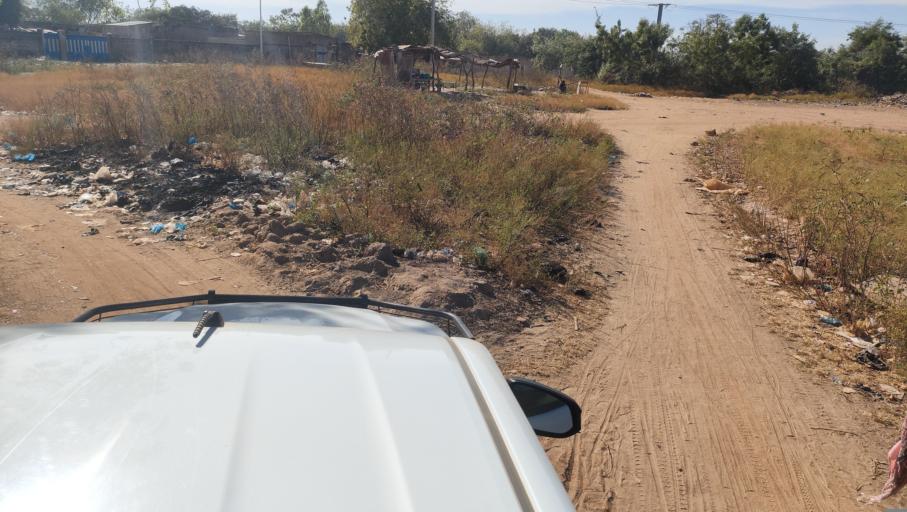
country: BF
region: Est
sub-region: Province du Gourma
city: Fada N'gourma
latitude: 12.0647
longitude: 0.3628
